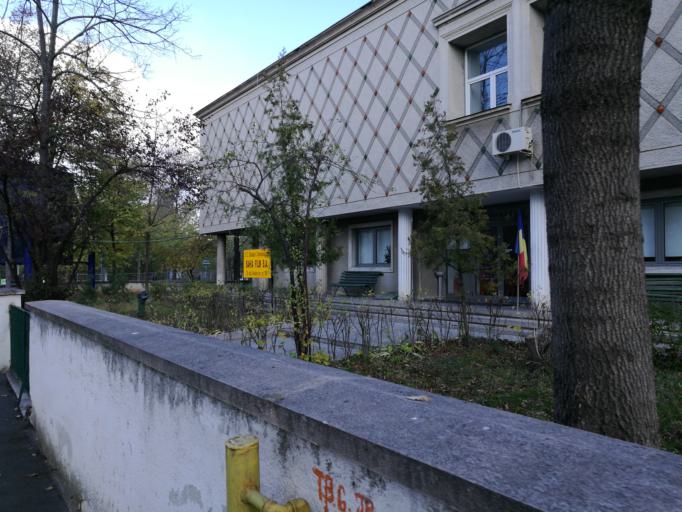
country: RO
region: Bucuresti
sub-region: Municipiul Bucuresti
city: Bucharest
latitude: 44.4707
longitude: 26.0881
